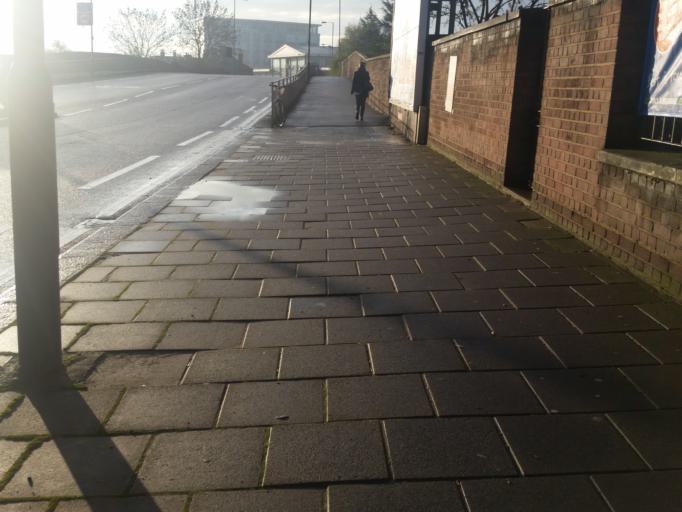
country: GB
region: England
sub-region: Greater London
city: Hammersmith
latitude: 51.5310
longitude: -0.2373
